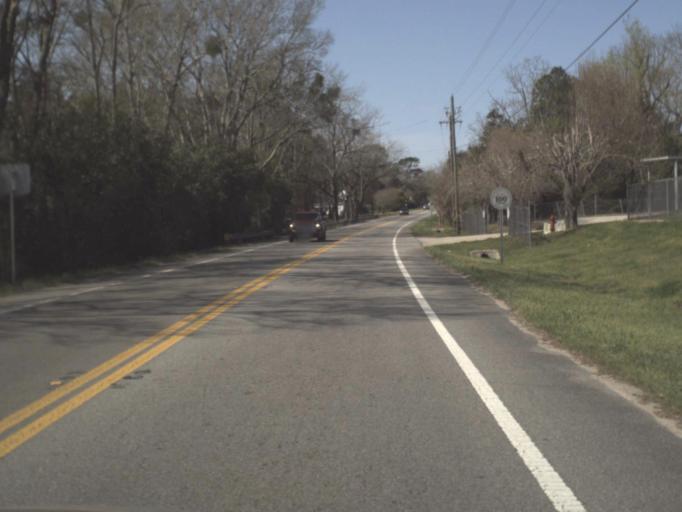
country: US
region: Florida
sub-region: Gadsden County
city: Gretna
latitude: 30.5693
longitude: -84.7361
